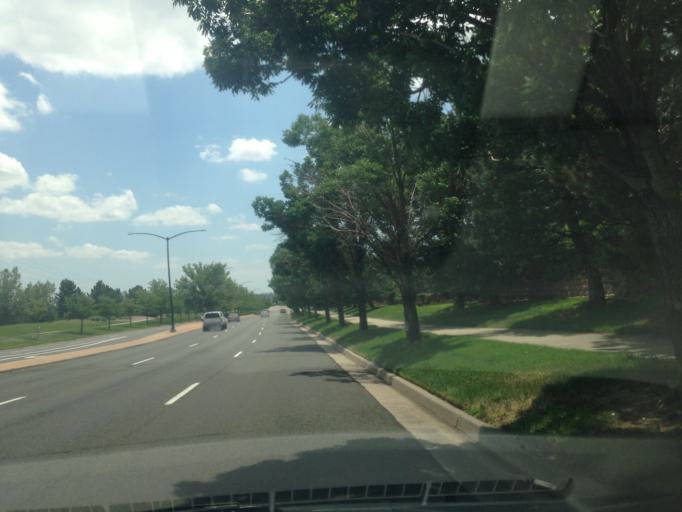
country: US
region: Colorado
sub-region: Broomfield County
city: Broomfield
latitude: 39.8972
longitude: -105.0725
